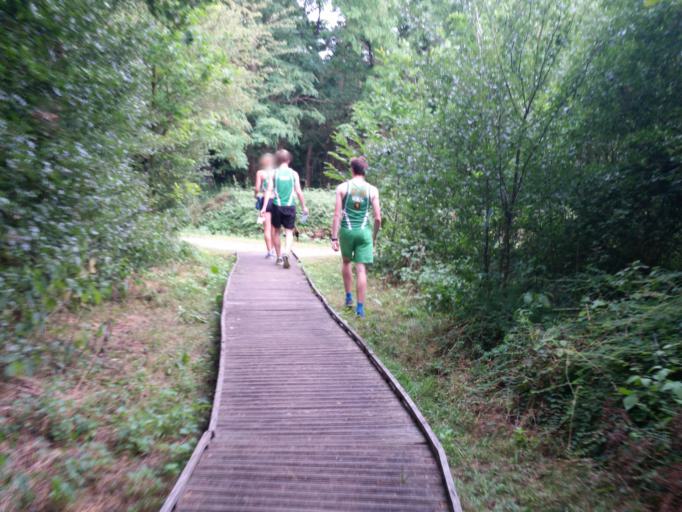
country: BE
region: Flanders
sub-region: Provincie Vlaams-Brabant
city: Zemst
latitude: 50.9783
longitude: 4.4855
